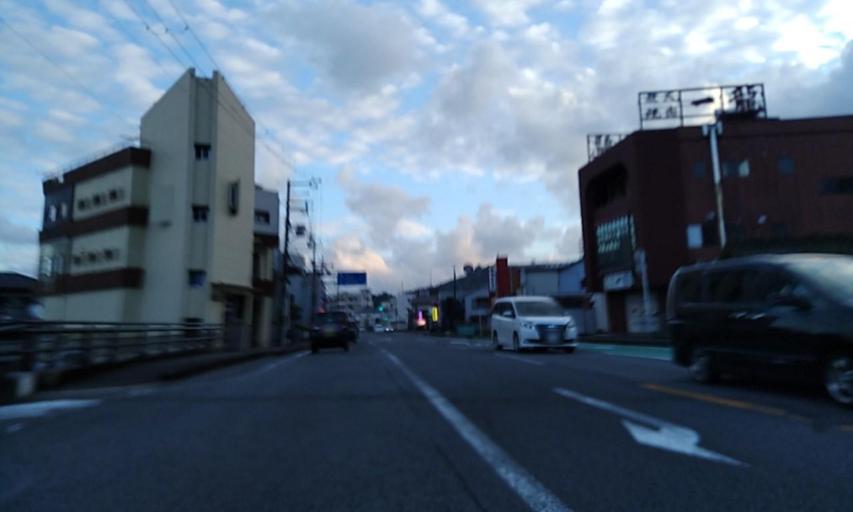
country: JP
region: Wakayama
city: Shingu
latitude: 33.7185
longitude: 135.9871
